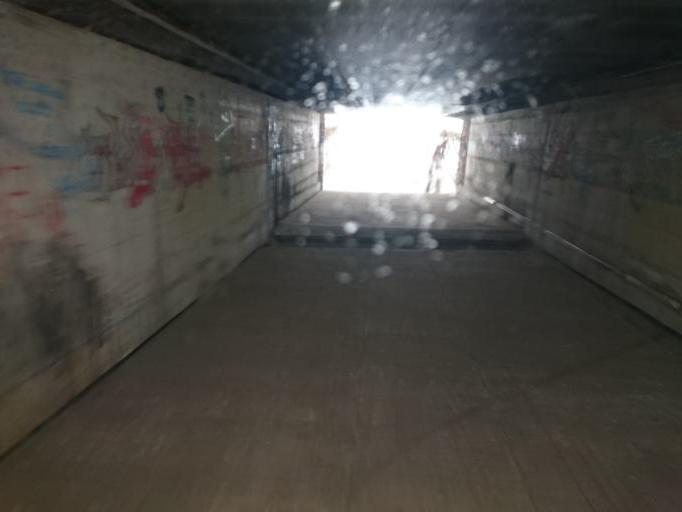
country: AT
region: Tyrol
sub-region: Politischer Bezirk Kufstein
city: Kufstein
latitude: 47.5840
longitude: 12.1538
